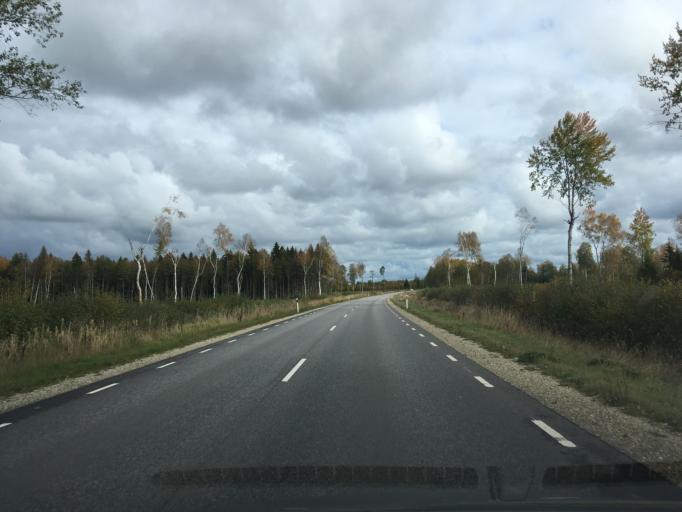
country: EE
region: Harju
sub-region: Anija vald
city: Kehra
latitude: 59.2435
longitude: 25.2989
